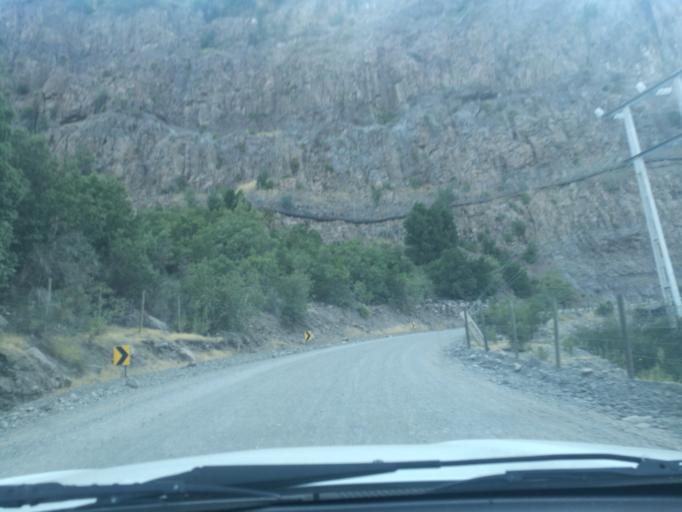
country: CL
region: O'Higgins
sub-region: Provincia de Cachapoal
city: Machali
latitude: -34.2831
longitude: -70.4400
